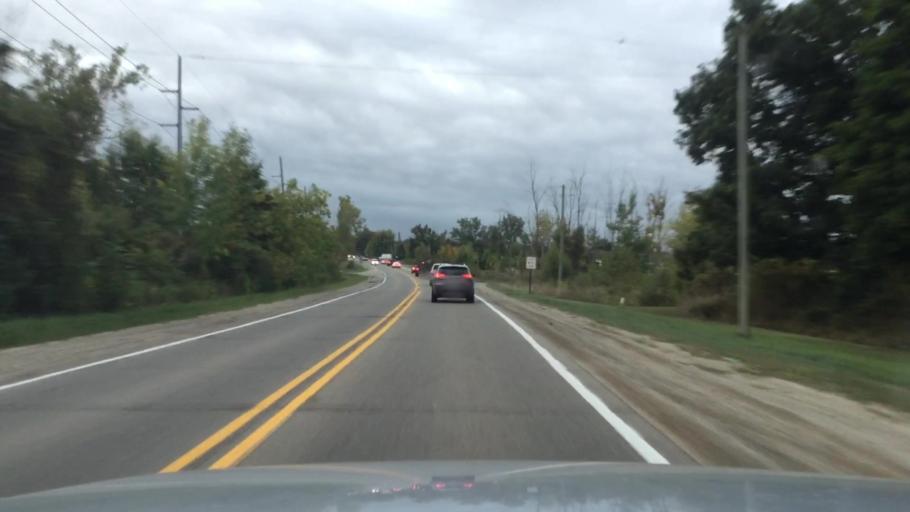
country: US
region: Michigan
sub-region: Livingston County
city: Brighton
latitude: 42.6223
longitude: -83.7519
